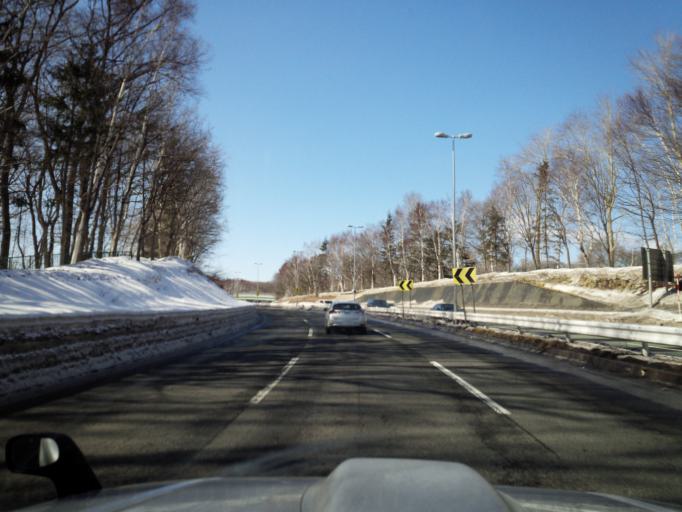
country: JP
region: Hokkaido
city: Sapporo
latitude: 43.0044
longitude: 141.4255
